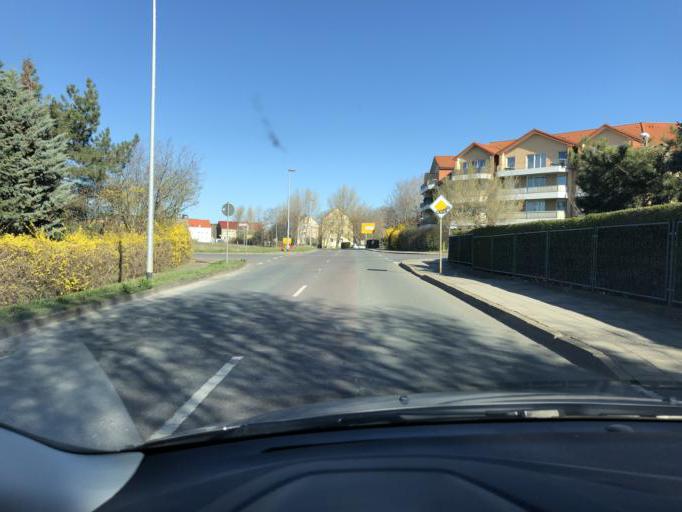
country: DE
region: Saxony-Anhalt
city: Stassfurt
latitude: 51.8583
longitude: 11.5954
